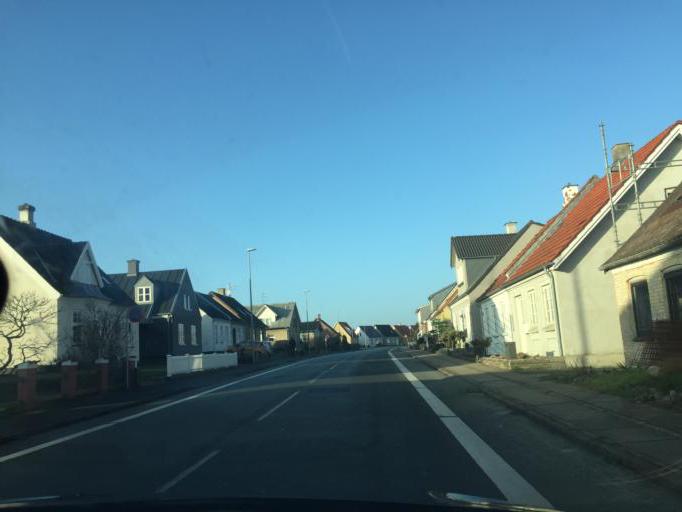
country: DK
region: South Denmark
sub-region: Faaborg-Midtfyn Kommune
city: Faaborg
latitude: 55.1027
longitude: 10.2281
